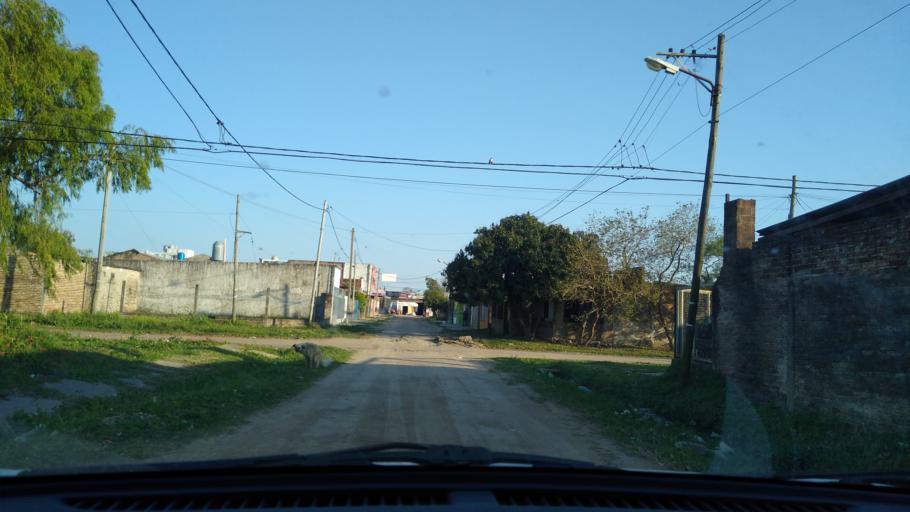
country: AR
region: Chaco
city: Resistencia
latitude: -27.4804
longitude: -58.9742
